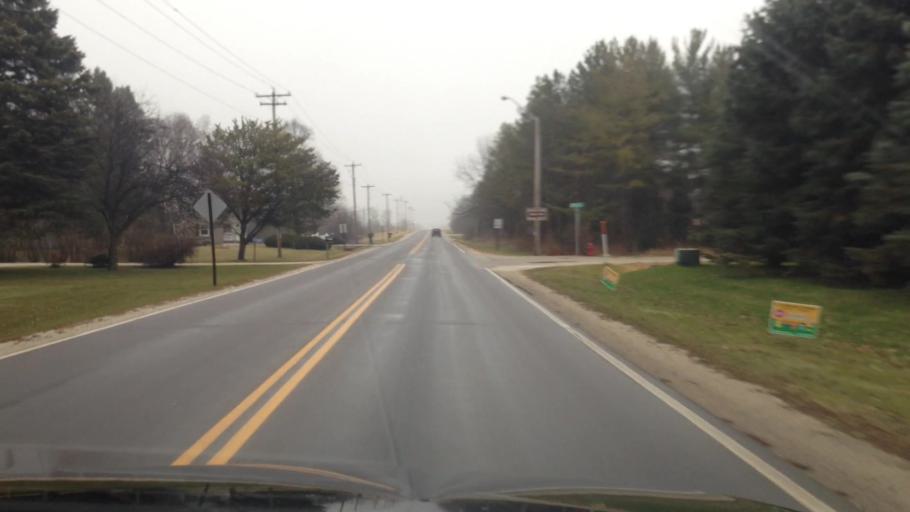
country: US
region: Wisconsin
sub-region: Washington County
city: Richfield
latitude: 43.2358
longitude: -88.1597
